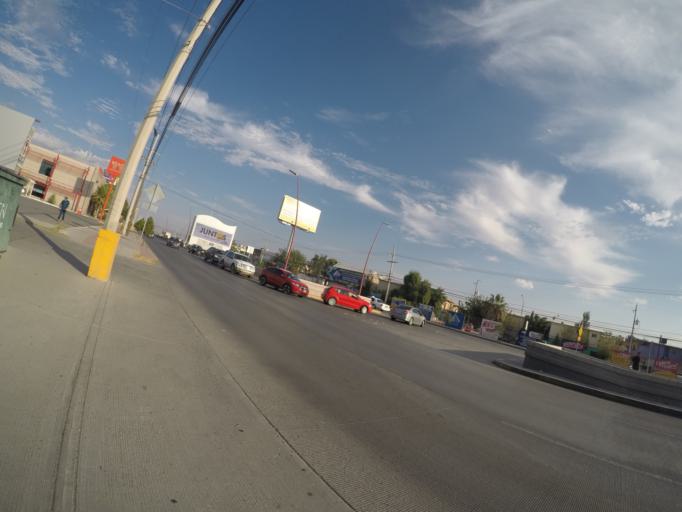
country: MX
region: Chihuahua
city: Ciudad Juarez
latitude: 31.6891
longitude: -106.4186
